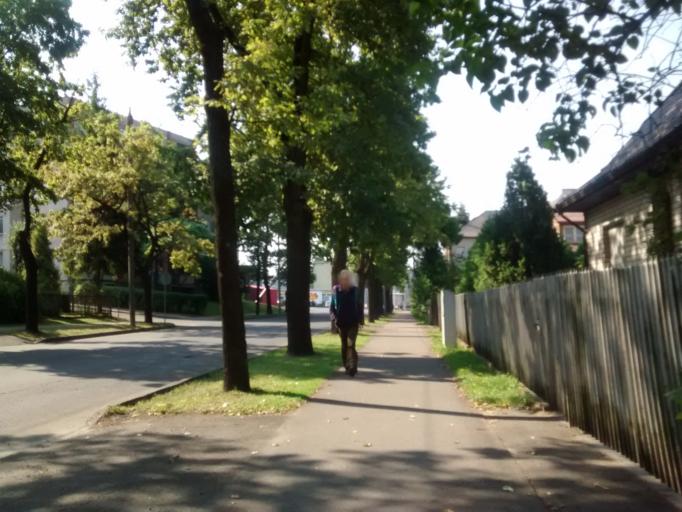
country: LT
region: Kauno apskritis
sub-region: Kaunas
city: Eiguliai
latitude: 54.9156
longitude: 23.9206
